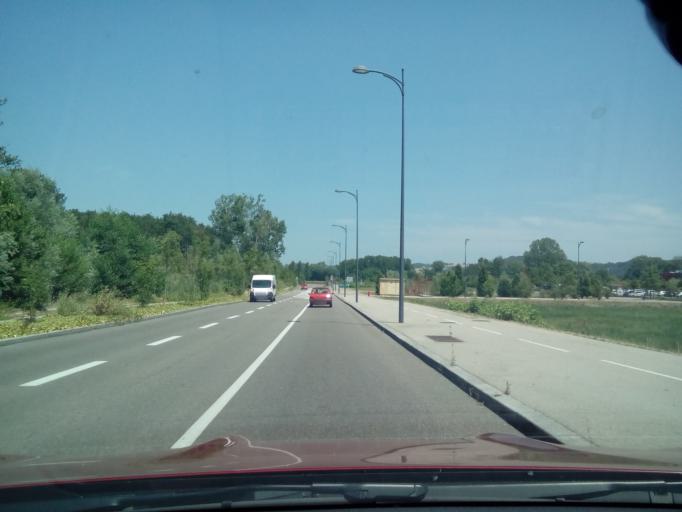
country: FR
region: Rhone-Alpes
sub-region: Departement de l'Isere
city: Domarin
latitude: 45.5984
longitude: 5.2443
